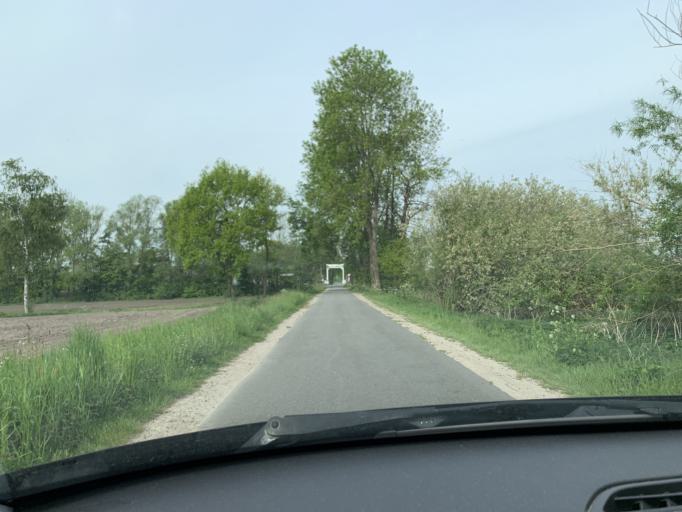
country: DE
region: Lower Saxony
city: Apen
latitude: 53.2090
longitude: 7.7597
